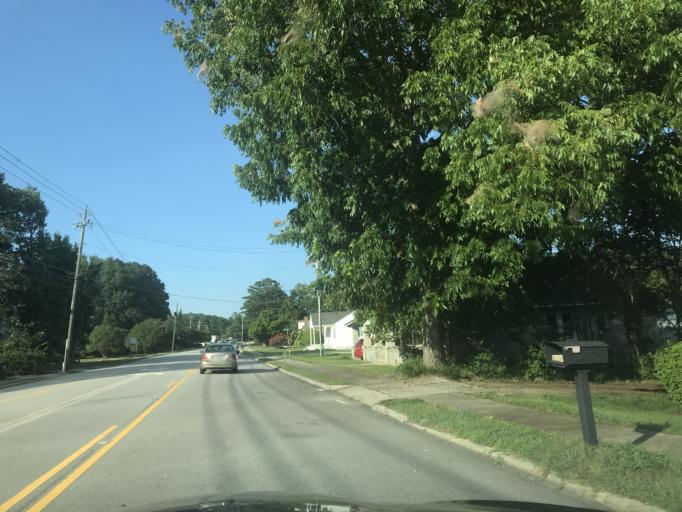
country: US
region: North Carolina
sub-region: Wake County
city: Rolesville
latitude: 35.9243
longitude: -78.4561
